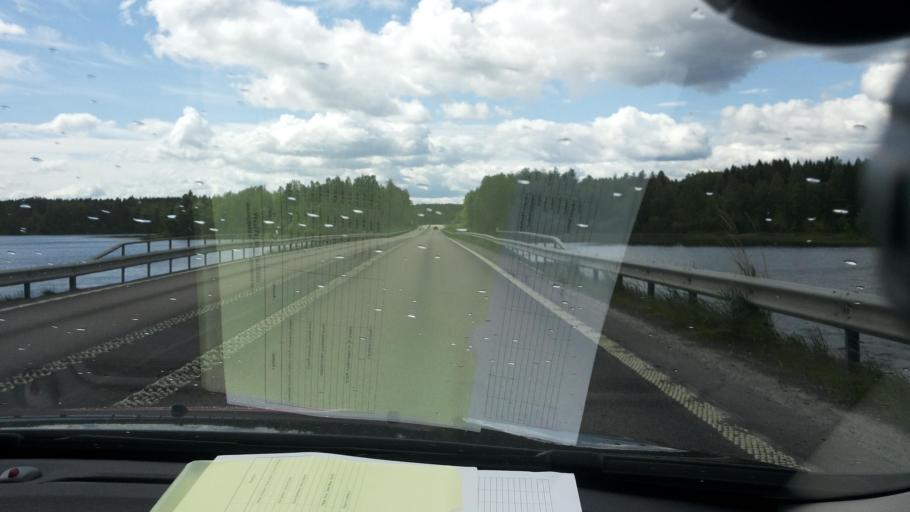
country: SE
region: Vaesternorrland
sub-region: Timra Kommun
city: Soraker
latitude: 62.5392
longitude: 17.5583
